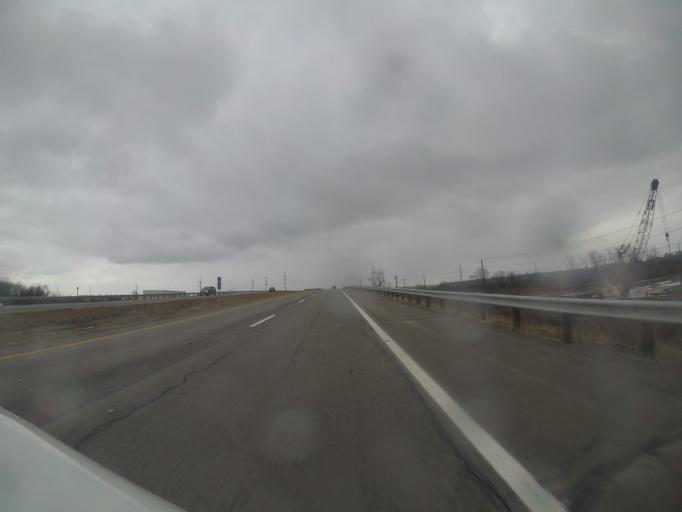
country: US
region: Ohio
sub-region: Wood County
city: Rossford
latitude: 41.5644
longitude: -83.5538
